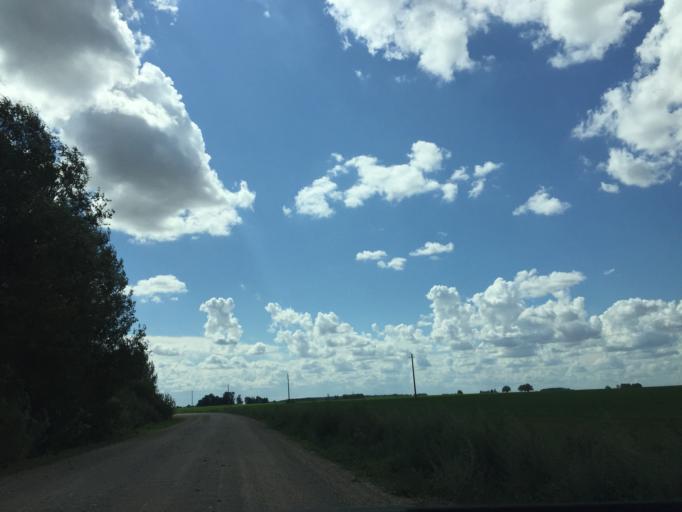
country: LV
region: Rundales
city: Pilsrundale
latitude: 56.3017
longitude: 23.9805
